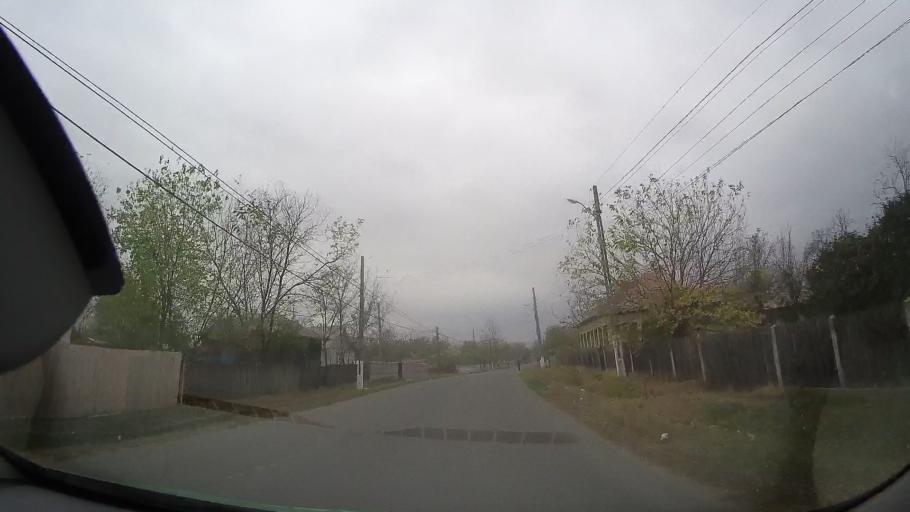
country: RO
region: Braila
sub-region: Comuna Ulmu
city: Jugureanu
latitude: 44.9420
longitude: 27.2816
